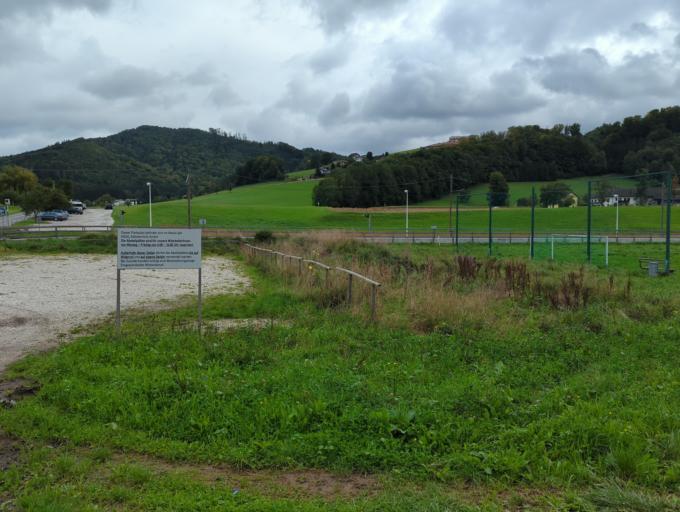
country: AT
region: Upper Austria
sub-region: Politischer Bezirk Gmunden
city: Gmunden
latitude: 47.9201
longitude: 13.8188
